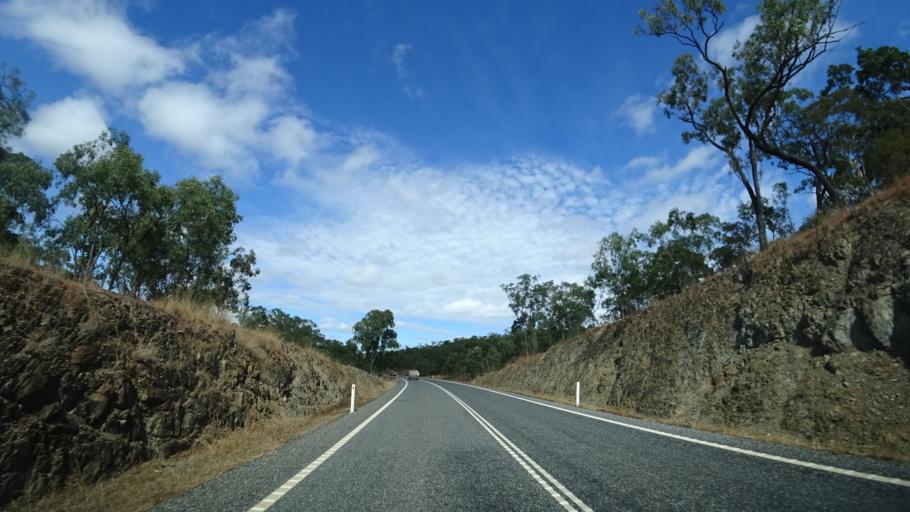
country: AU
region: Queensland
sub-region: Cairns
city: Port Douglas
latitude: -16.2735
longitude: 144.7145
